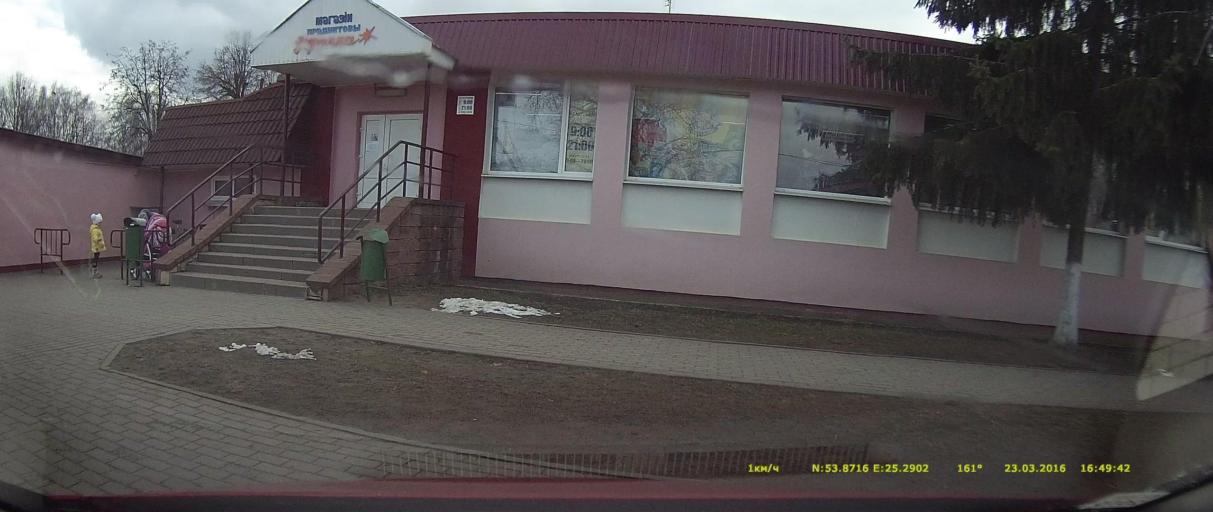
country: BY
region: Grodnenskaya
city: Lida
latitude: 53.8766
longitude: 25.2869
